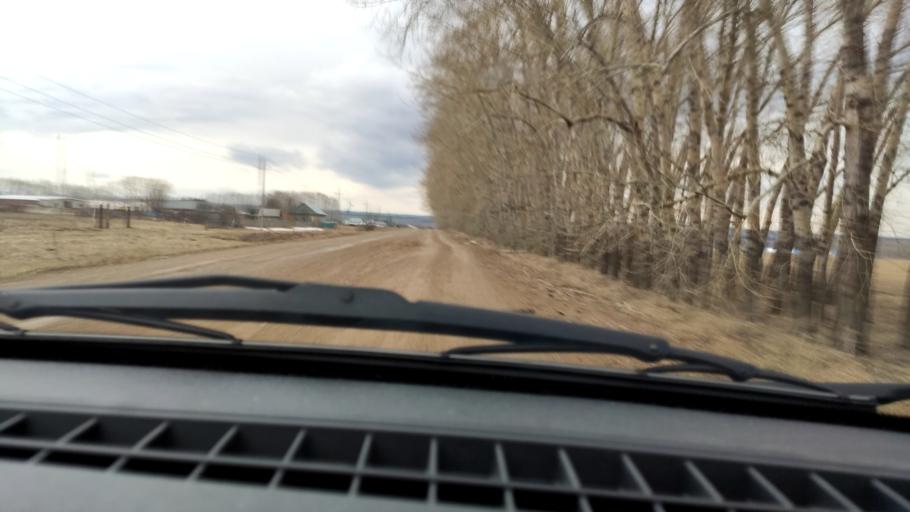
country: RU
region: Bashkortostan
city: Semiletka
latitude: 55.2885
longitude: 54.6759
